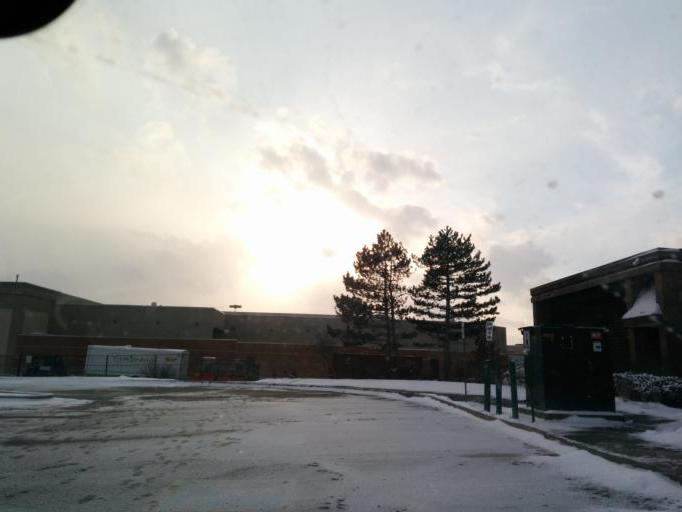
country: CA
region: Ontario
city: Mississauga
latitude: 43.5828
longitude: -79.7576
